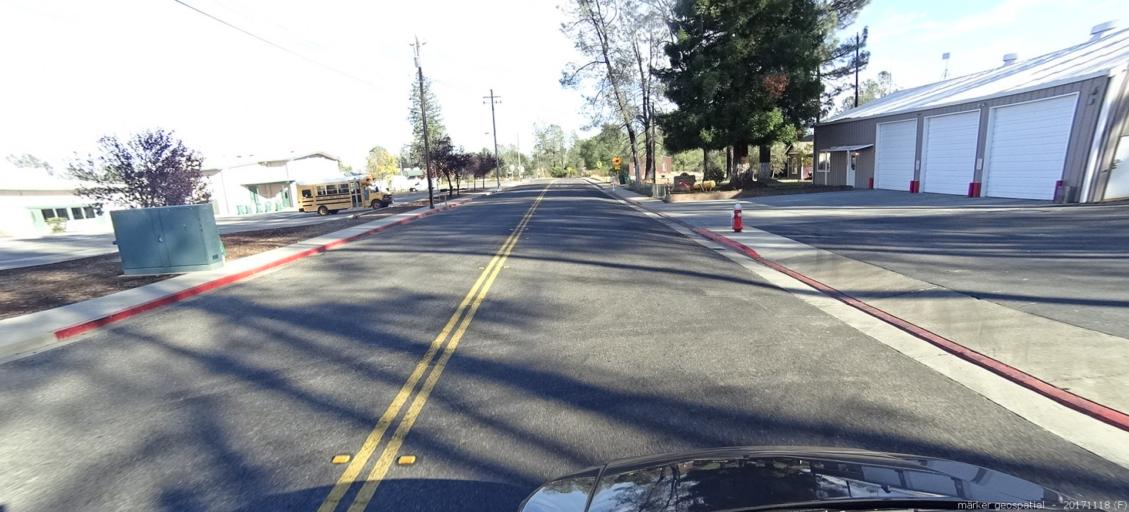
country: US
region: California
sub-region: Shasta County
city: Anderson
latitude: 40.4466
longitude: -122.4099
